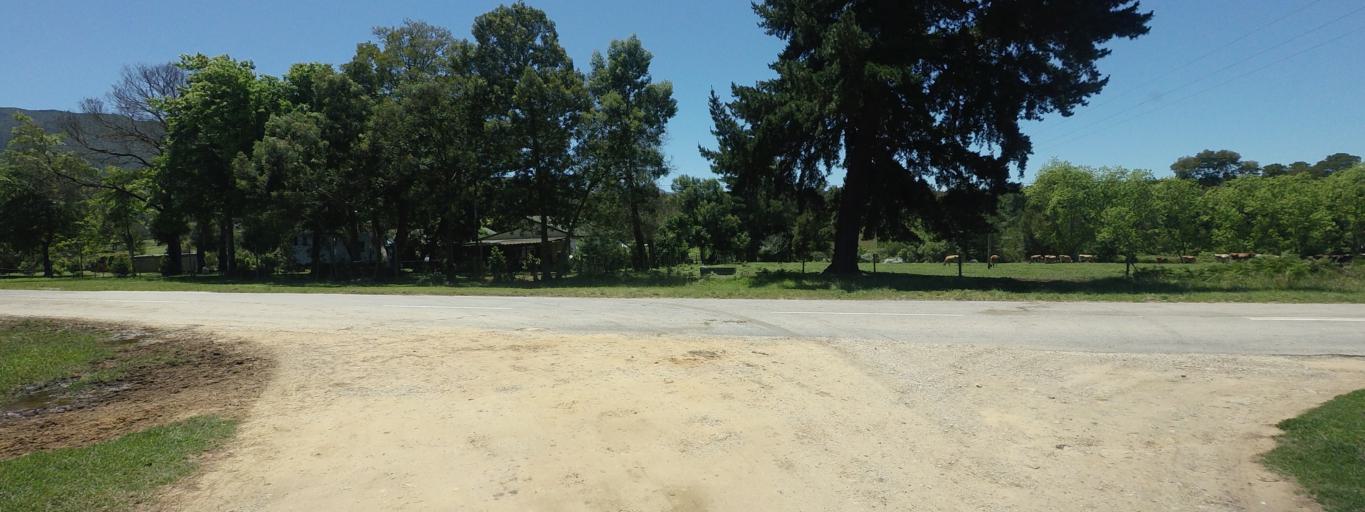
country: ZA
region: Western Cape
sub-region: Eden District Municipality
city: Plettenberg Bay
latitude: -33.9434
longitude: 23.5116
